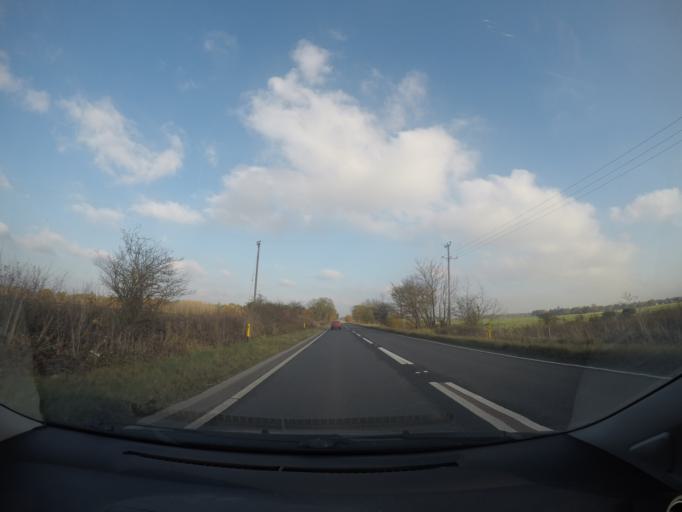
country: GB
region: England
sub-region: City of York
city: Murton
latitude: 54.0053
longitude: -1.0077
